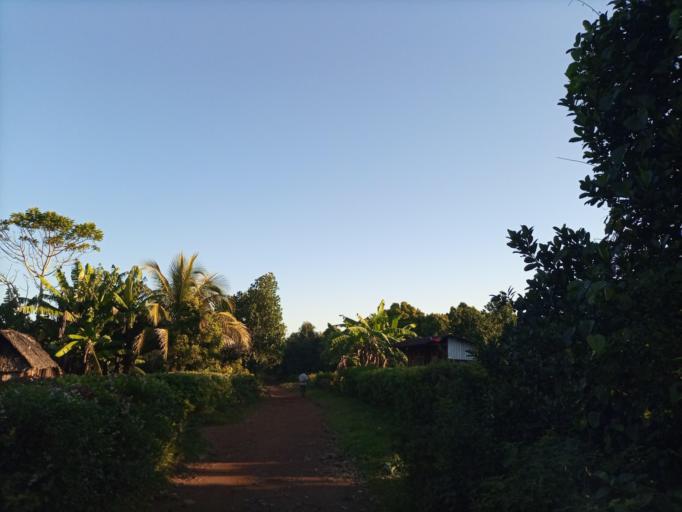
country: MG
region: Atsimo-Atsinanana
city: Vohipaho
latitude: -23.5224
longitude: 47.6215
